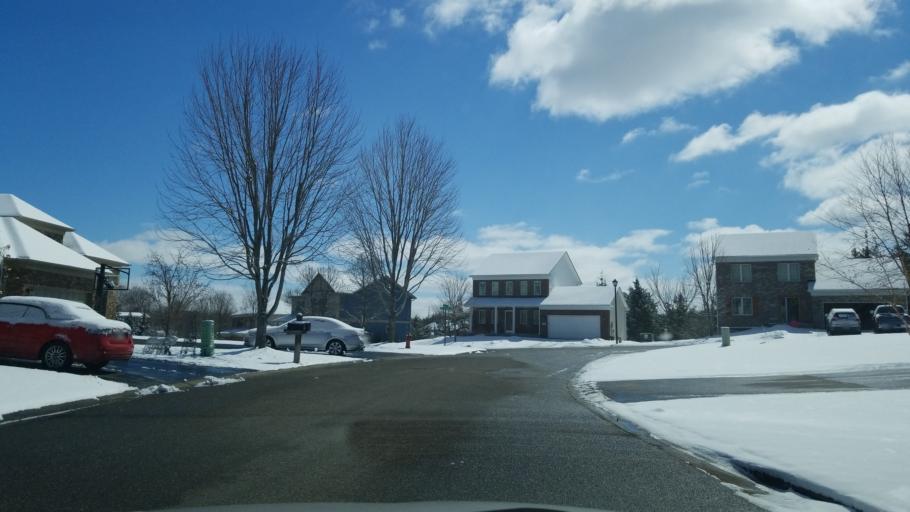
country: US
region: Wisconsin
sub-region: Saint Croix County
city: Hudson
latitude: 44.9590
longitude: -92.7058
